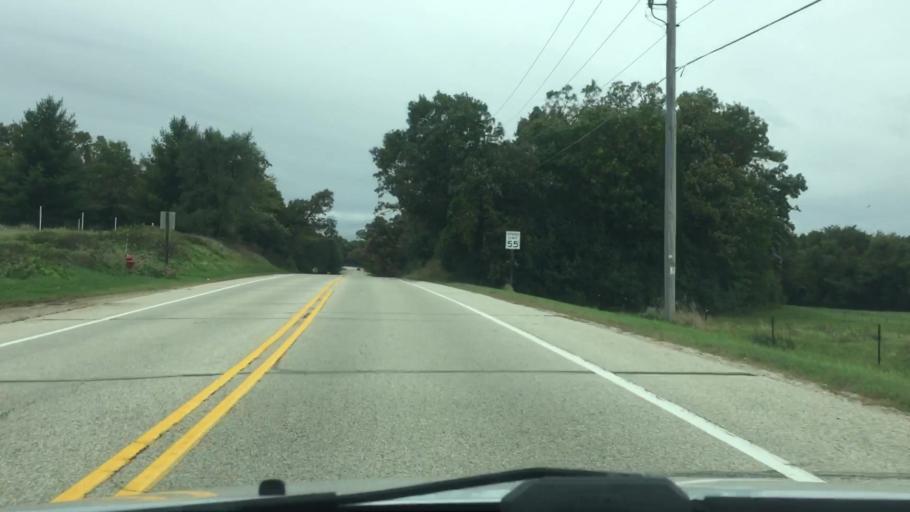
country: US
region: Wisconsin
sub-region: Waukesha County
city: Eagle
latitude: 42.8681
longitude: -88.4861
